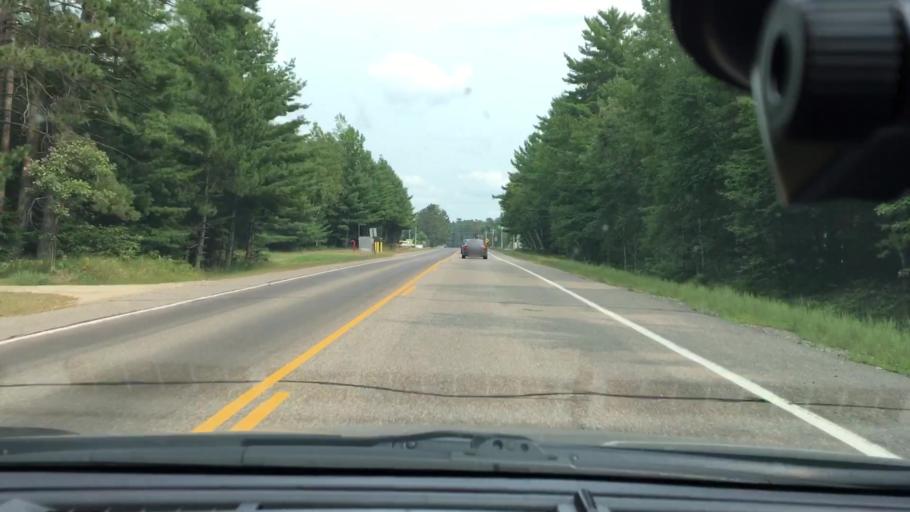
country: US
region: Minnesota
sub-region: Crow Wing County
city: Cross Lake
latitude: 46.7308
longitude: -93.9692
